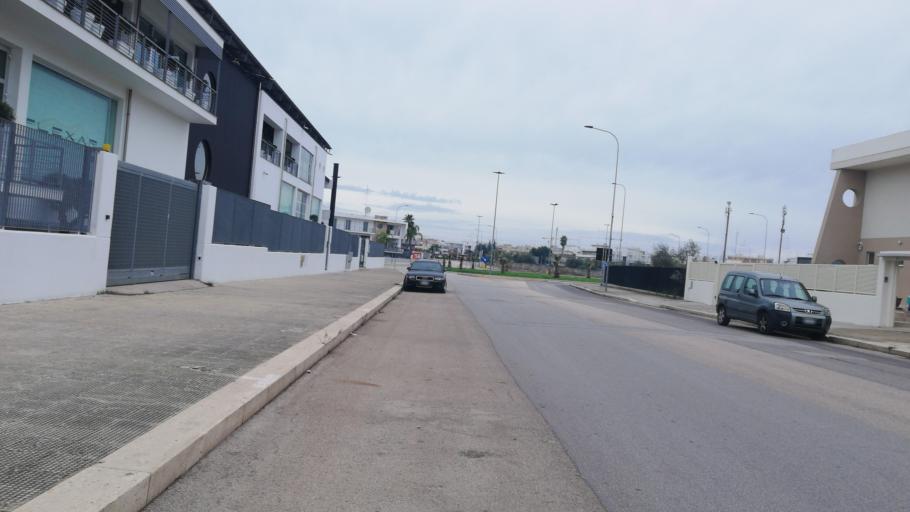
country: IT
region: Apulia
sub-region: Provincia di Bari
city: Bitonto
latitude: 41.1170
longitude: 16.6815
